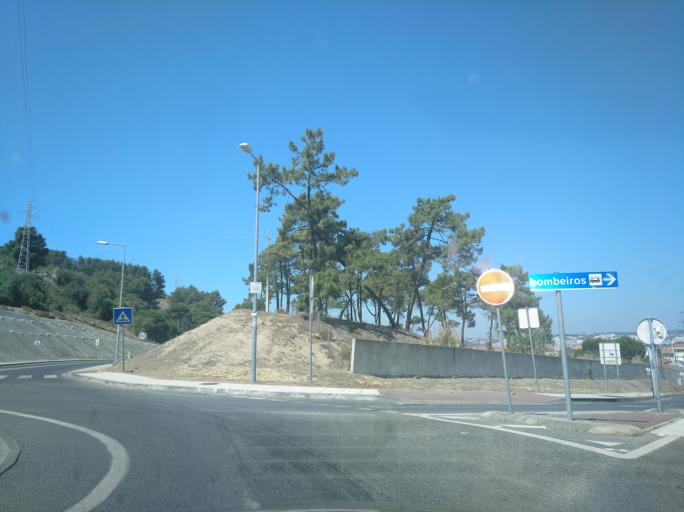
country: PT
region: Setubal
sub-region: Almada
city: Trafaria
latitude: 38.6664
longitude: -9.2313
